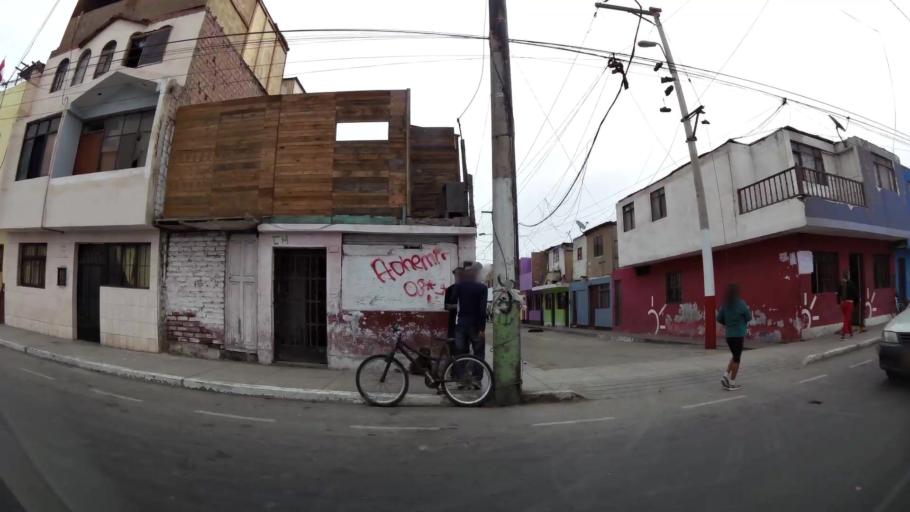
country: PE
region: Callao
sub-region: Callao
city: Callao
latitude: -12.0676
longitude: -77.1344
